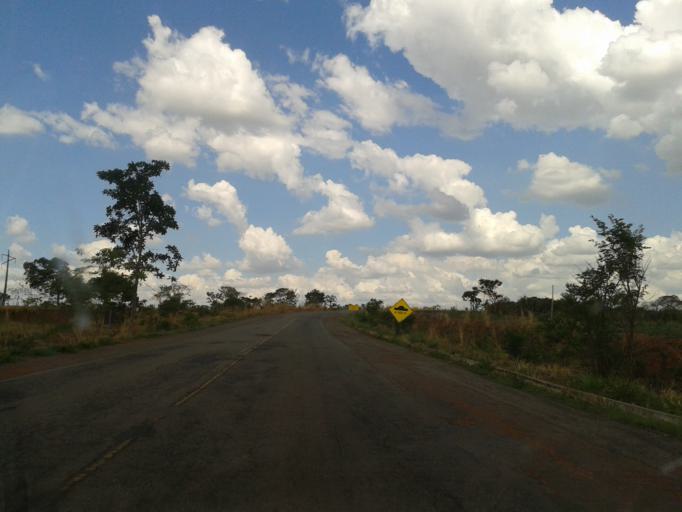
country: BR
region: Goias
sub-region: Caldas Novas
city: Caldas Novas
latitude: -17.6975
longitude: -48.7158
